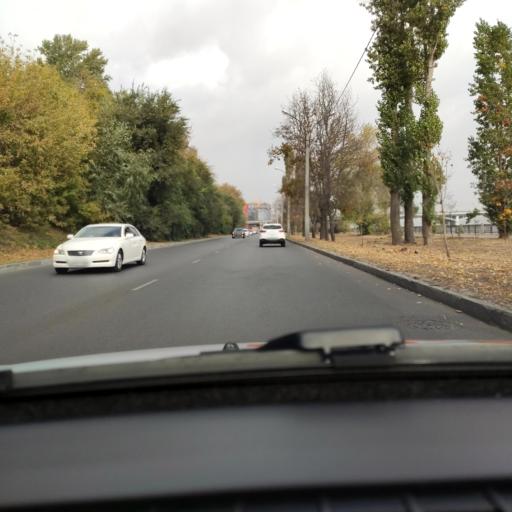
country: RU
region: Voronezj
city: Voronezh
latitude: 51.6643
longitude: 39.2199
